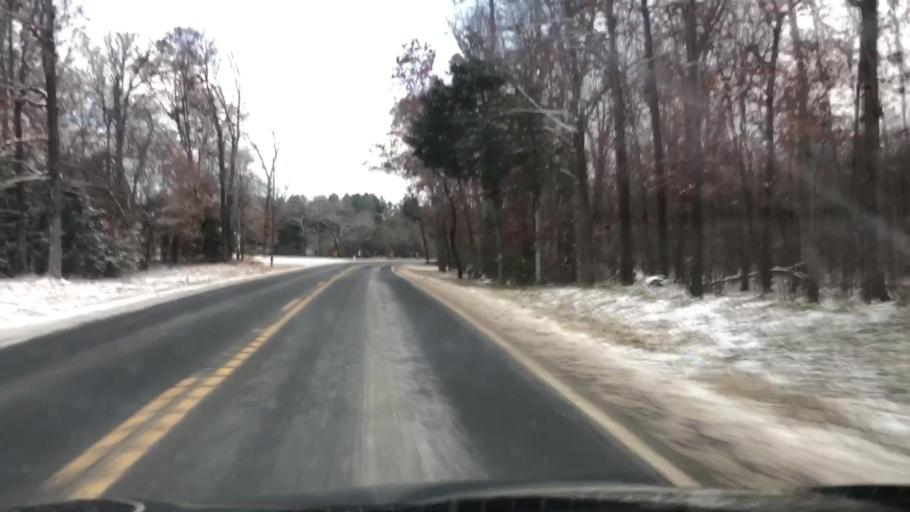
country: US
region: Virginia
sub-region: Fauquier County
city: Bealeton
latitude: 38.5959
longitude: -77.7499
